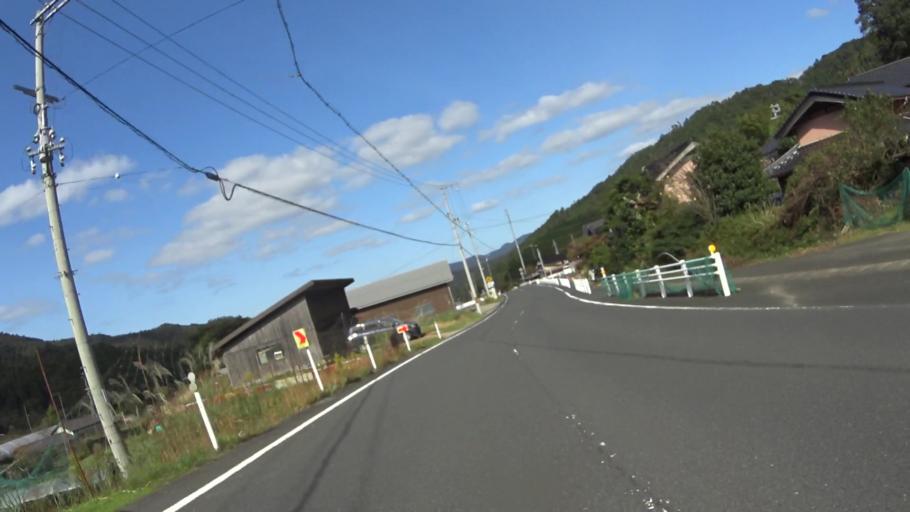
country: JP
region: Hyogo
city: Toyooka
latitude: 35.5435
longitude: 134.9778
